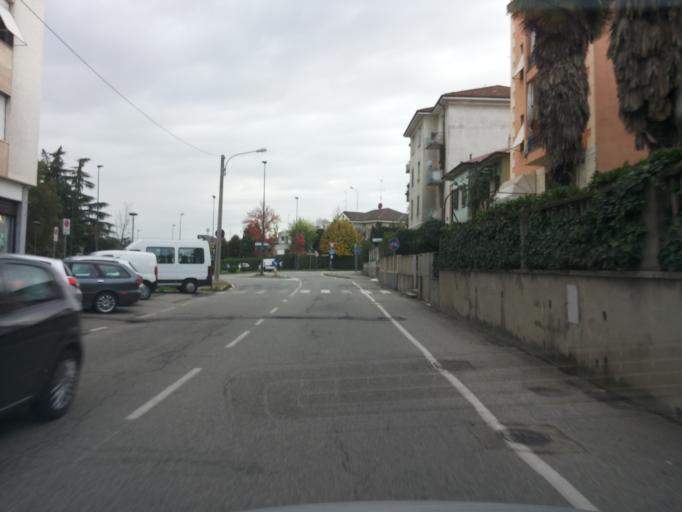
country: IT
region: Piedmont
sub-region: Provincia di Alessandria
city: Casale Monferrato
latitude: 45.1225
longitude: 8.4448
